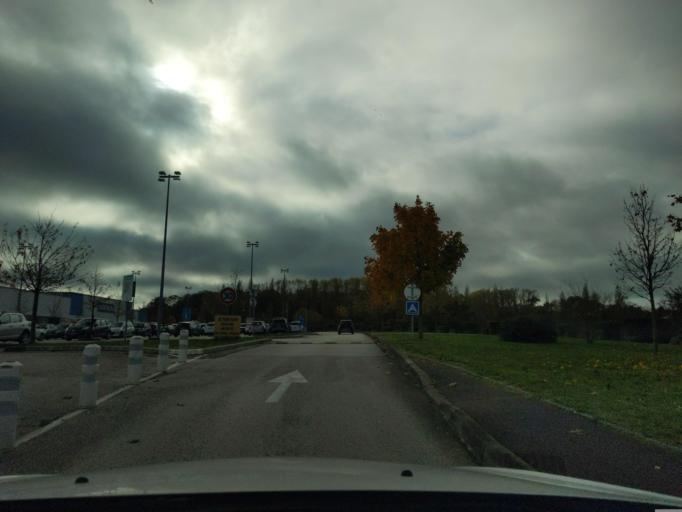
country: FR
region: Bourgogne
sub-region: Departement de la Cote-d'Or
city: Saint-Apollinaire
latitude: 47.3164
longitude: 5.0880
